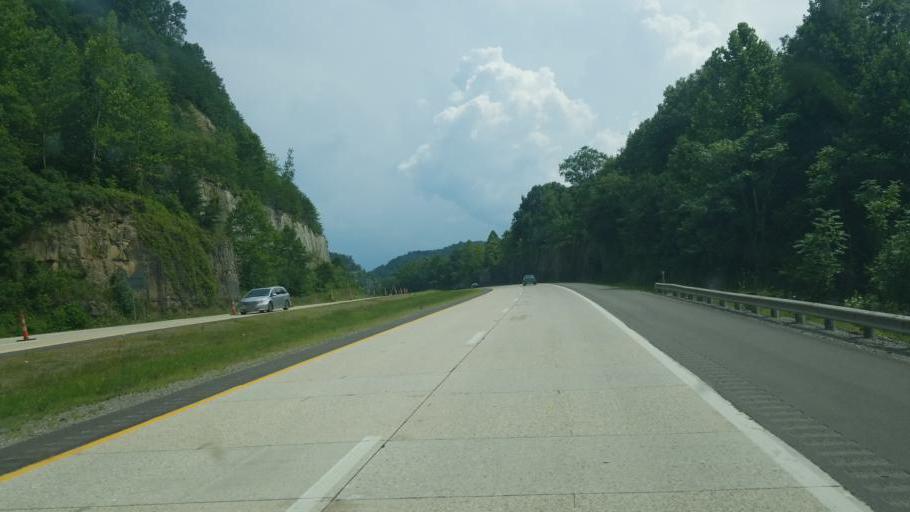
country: US
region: West Virginia
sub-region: Kanawha County
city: Alum Creek
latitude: 38.2204
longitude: -81.8346
